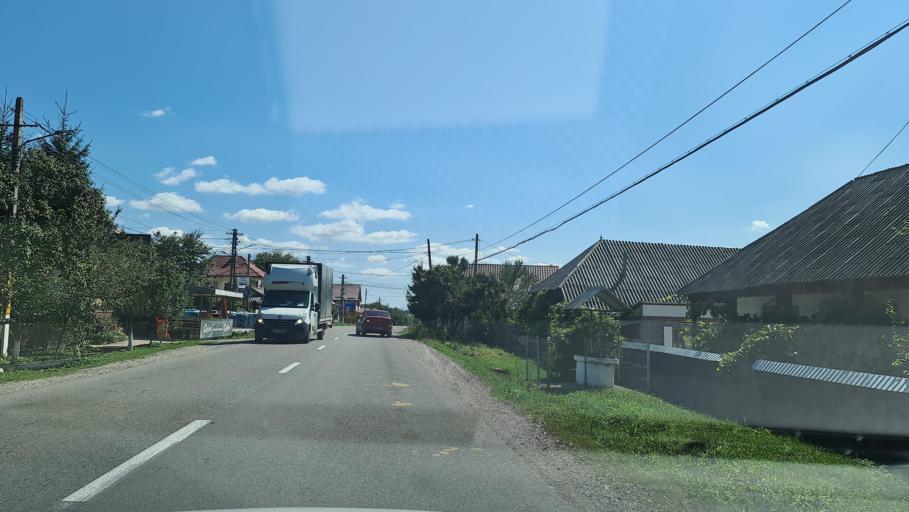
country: RO
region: Bacau
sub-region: Comuna Balcani
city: Balcani
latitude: 46.6465
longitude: 26.5657
